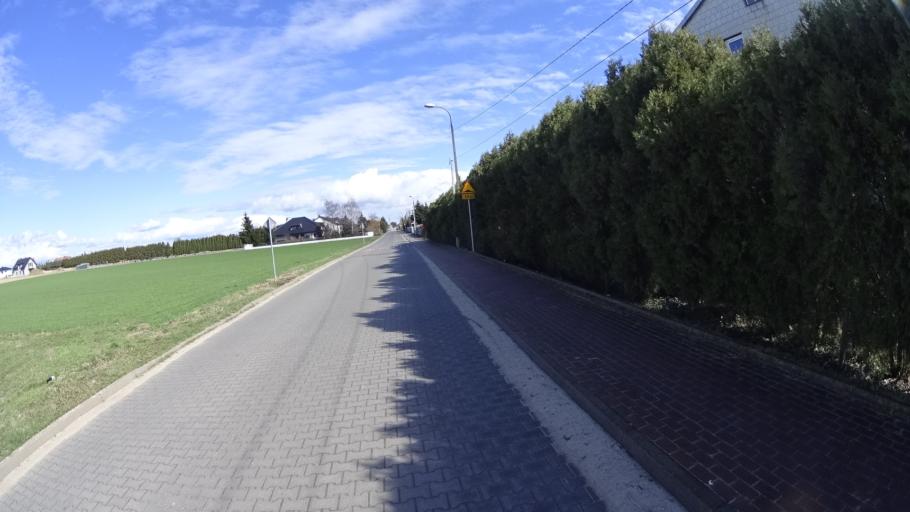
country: PL
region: Masovian Voivodeship
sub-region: Powiat warszawski zachodni
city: Jozefow
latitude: 52.2040
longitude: 20.6986
